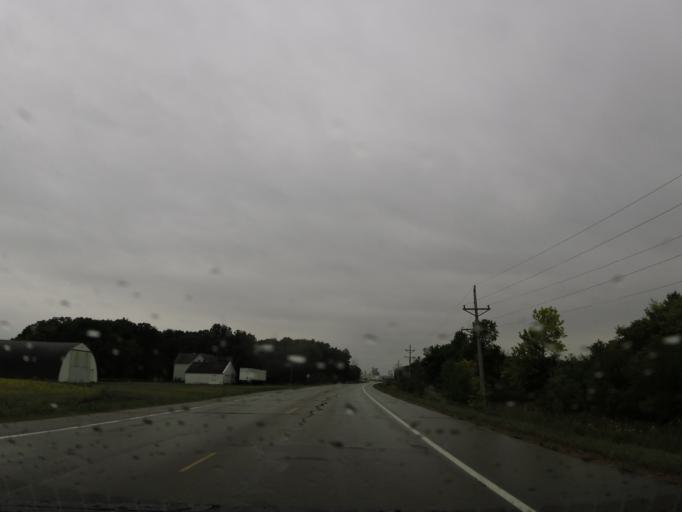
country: US
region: Minnesota
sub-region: Marshall County
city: Warren
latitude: 48.4459
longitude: -96.8672
